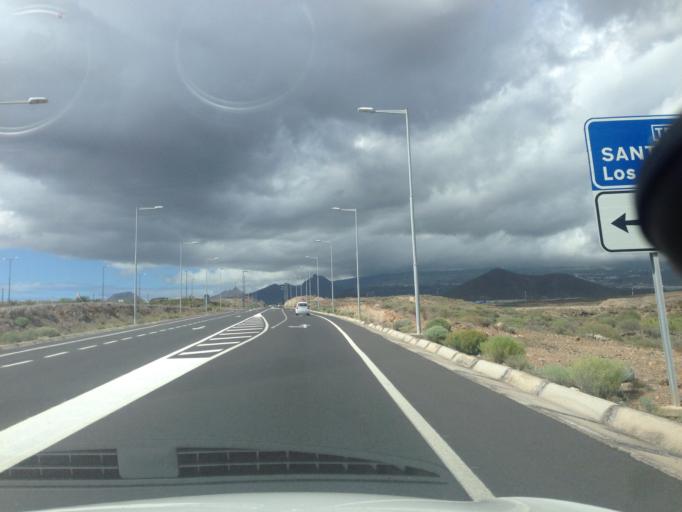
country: ES
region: Canary Islands
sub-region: Provincia de Santa Cruz de Tenerife
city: Las Rosas
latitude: 28.0364
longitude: -16.6002
